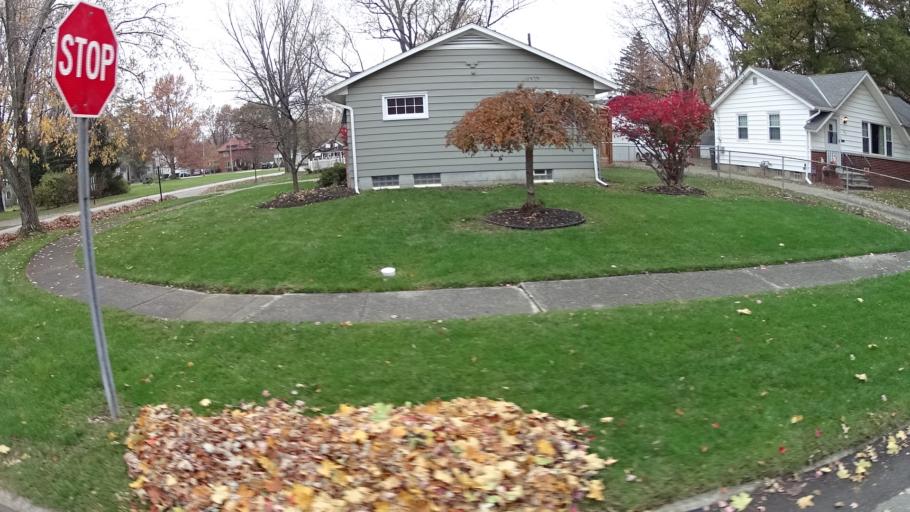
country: US
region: Ohio
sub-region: Lorain County
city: Elyria
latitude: 41.3547
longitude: -82.0984
